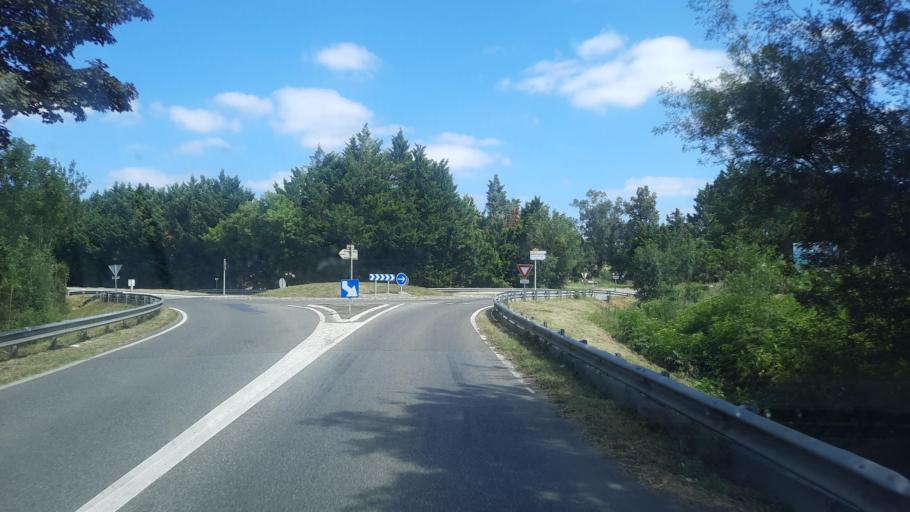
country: FR
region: Midi-Pyrenees
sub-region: Departement du Gers
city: Samatan
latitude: 43.4967
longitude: 0.9680
